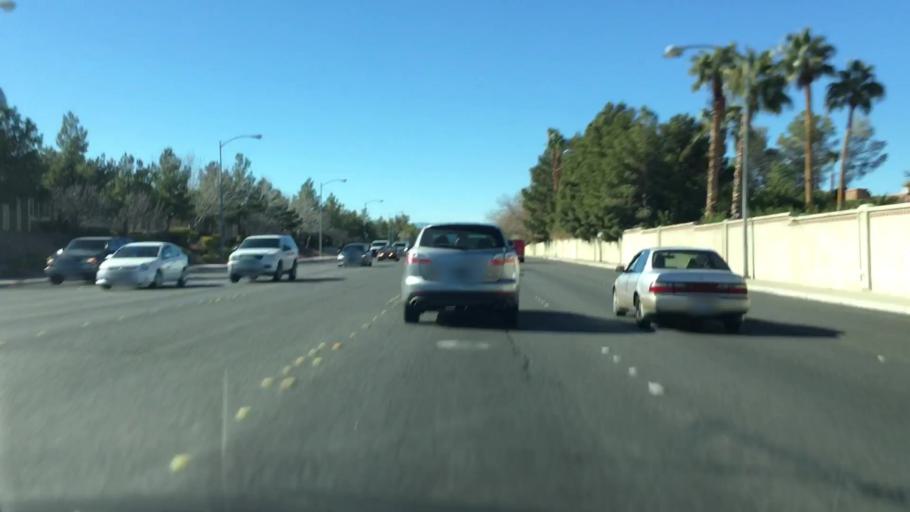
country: US
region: Nevada
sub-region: Clark County
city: Whitney
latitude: 36.0571
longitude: -115.1024
